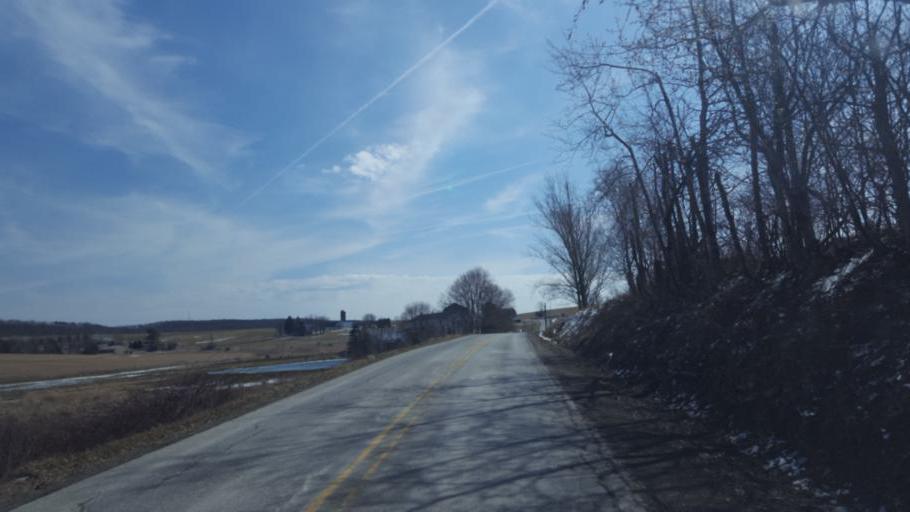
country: US
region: Pennsylvania
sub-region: Potter County
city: Galeton
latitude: 41.8916
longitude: -77.7445
